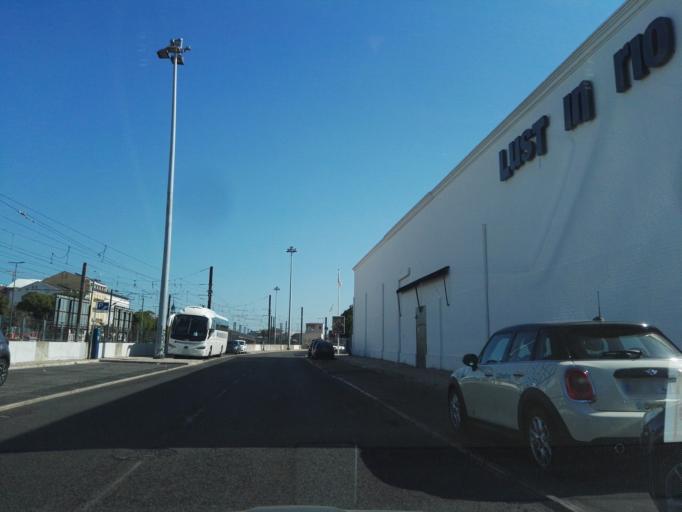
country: PT
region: Setubal
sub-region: Almada
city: Cacilhas
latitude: 38.7061
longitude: -9.1503
